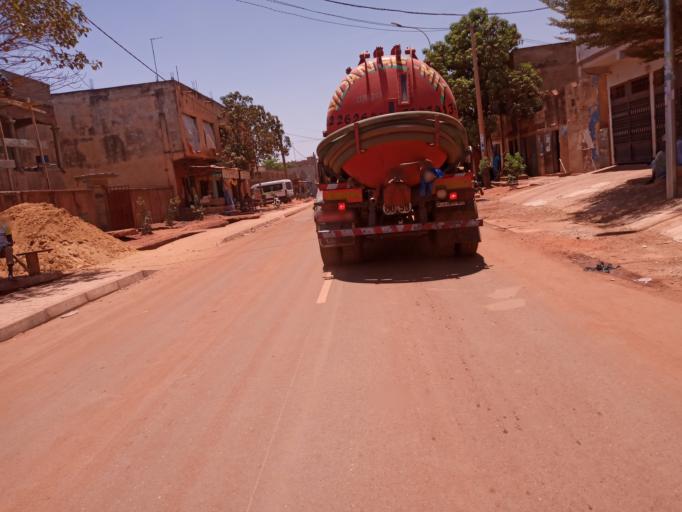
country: ML
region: Bamako
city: Bamako
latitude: 12.5910
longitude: -7.9827
